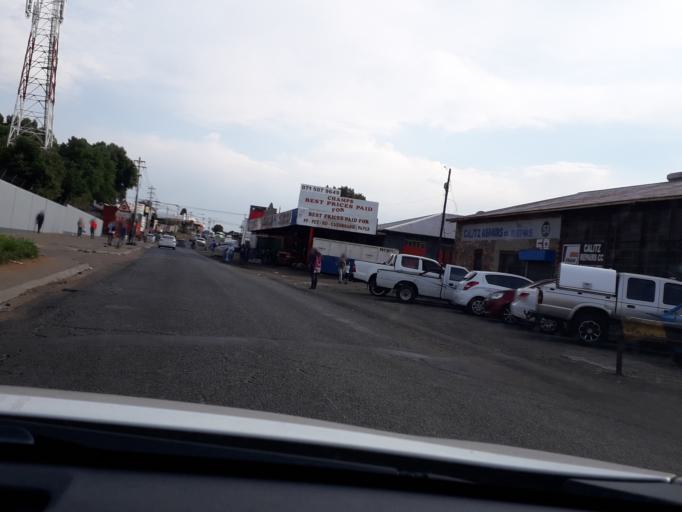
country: ZA
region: Gauteng
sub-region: City of Johannesburg Metropolitan Municipality
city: Johannesburg
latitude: -26.1781
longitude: 27.9666
